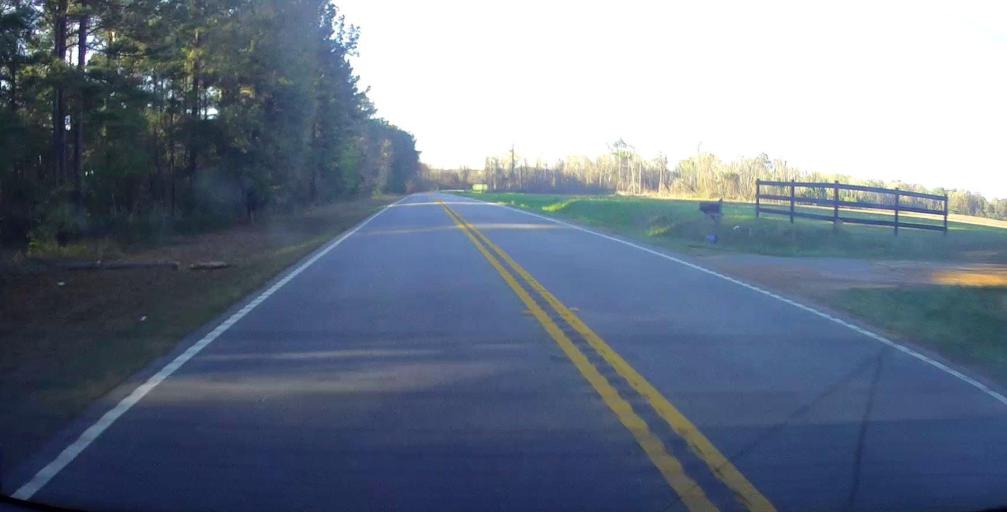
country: US
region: Georgia
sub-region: Pulaski County
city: Hawkinsville
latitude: 32.1686
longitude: -83.3608
